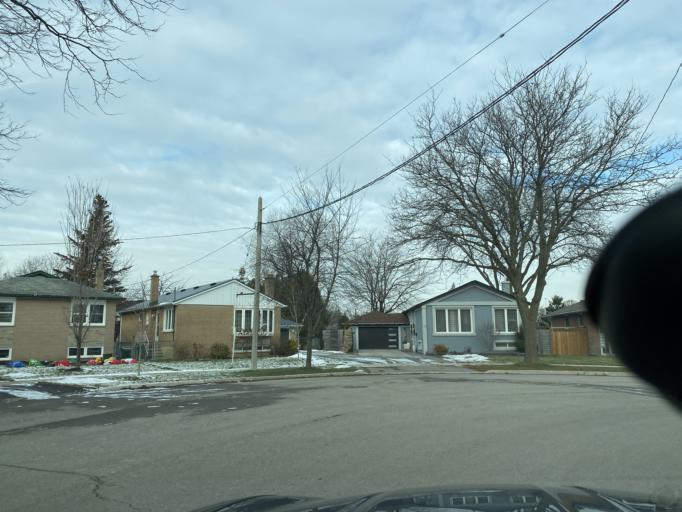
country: CA
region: Ontario
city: Etobicoke
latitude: 43.6656
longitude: -79.5772
